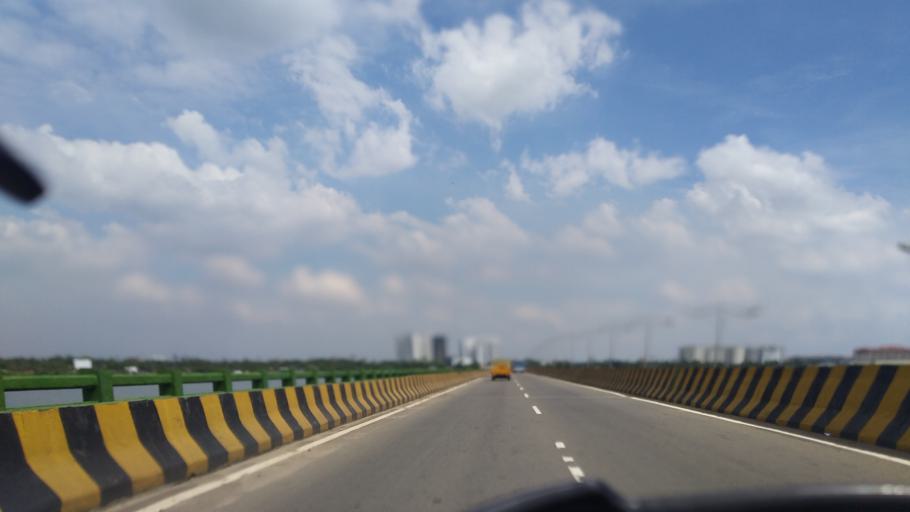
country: IN
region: Kerala
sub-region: Ernakulam
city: Cochin
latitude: 9.9893
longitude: 76.2589
